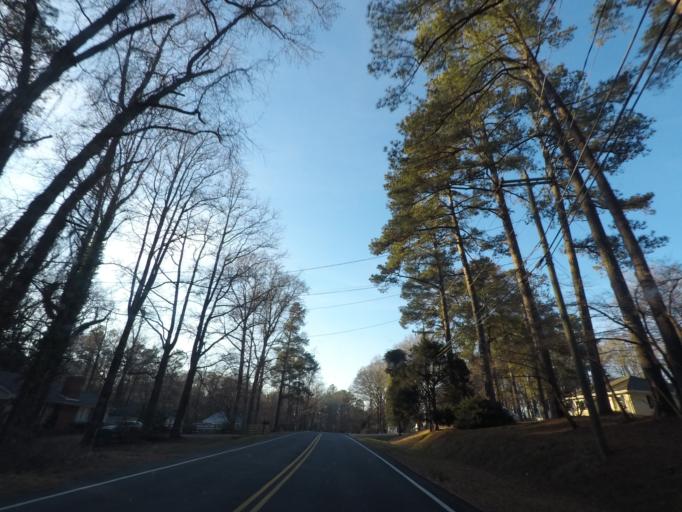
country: US
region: North Carolina
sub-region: Durham County
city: Durham
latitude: 36.0450
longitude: -78.9656
